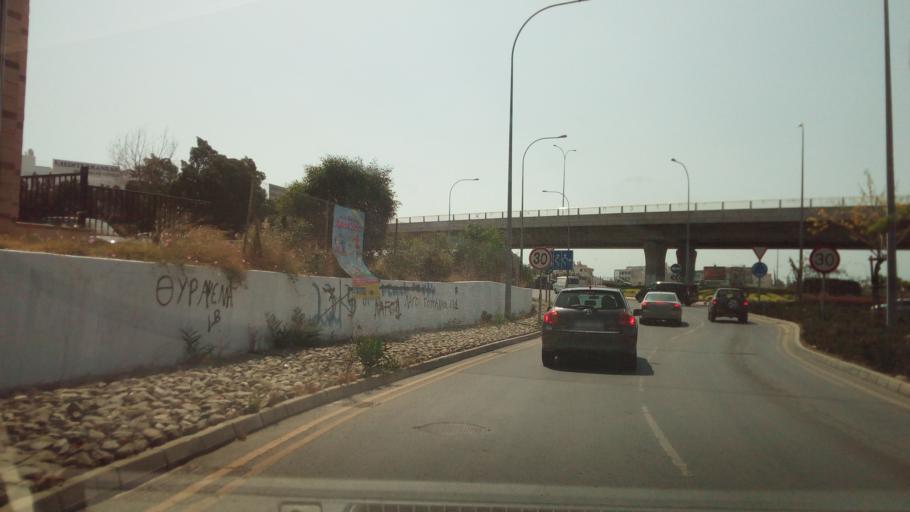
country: CY
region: Limassol
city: Limassol
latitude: 34.7054
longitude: 33.0267
